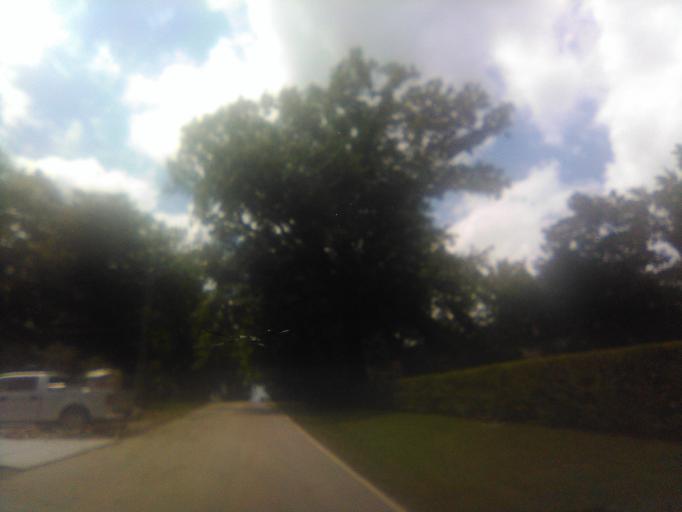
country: US
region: Tennessee
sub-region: Davidson County
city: Belle Meade
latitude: 36.1015
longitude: -86.8462
